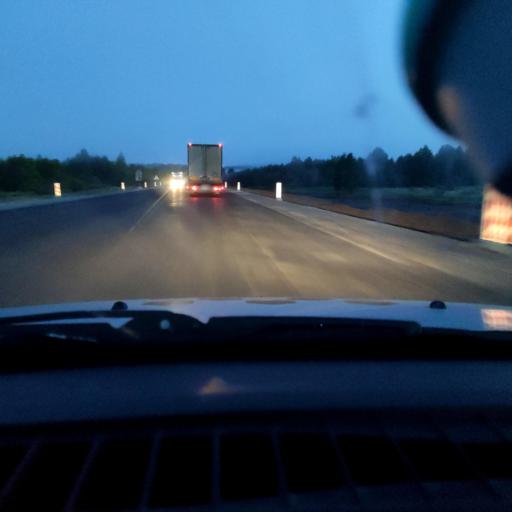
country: RU
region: Sverdlovsk
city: Bisert'
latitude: 56.8350
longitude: 58.9113
